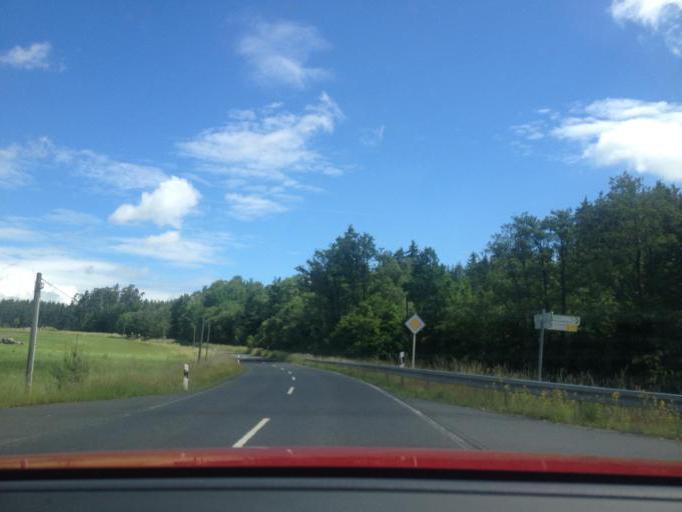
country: DE
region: Bavaria
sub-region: Upper Palatinate
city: Pechbrunn
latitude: 49.9734
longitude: 12.1772
